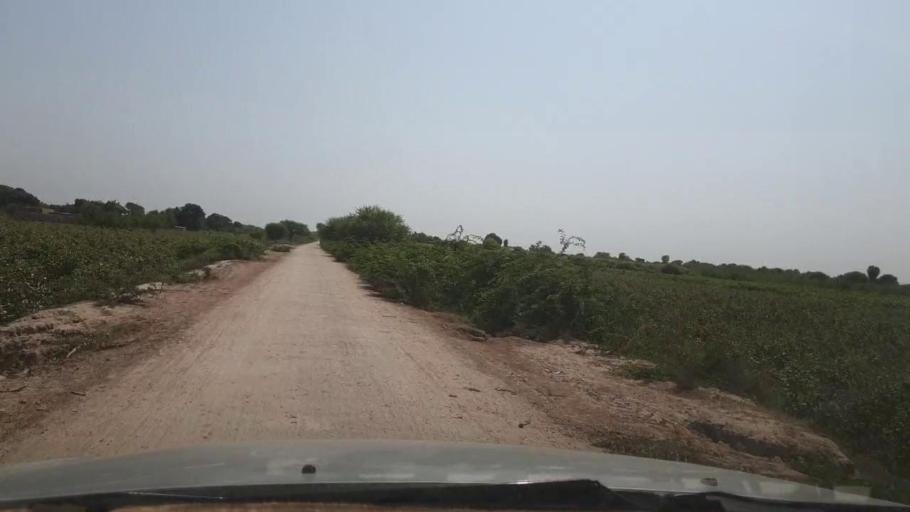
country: PK
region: Sindh
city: Tando Ghulam Ali
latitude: 25.1585
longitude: 68.8950
